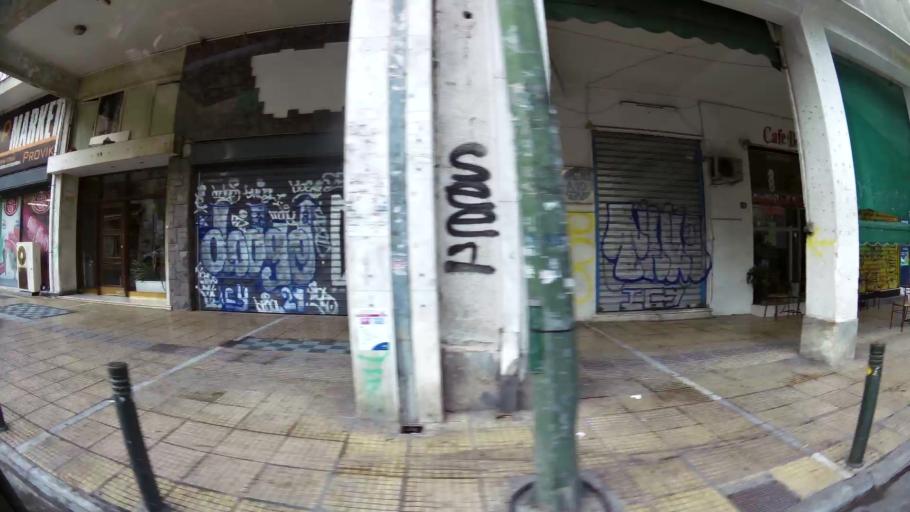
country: GR
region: Attica
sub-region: Nomarchia Athinas
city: Athens
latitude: 37.9888
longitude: 23.7251
